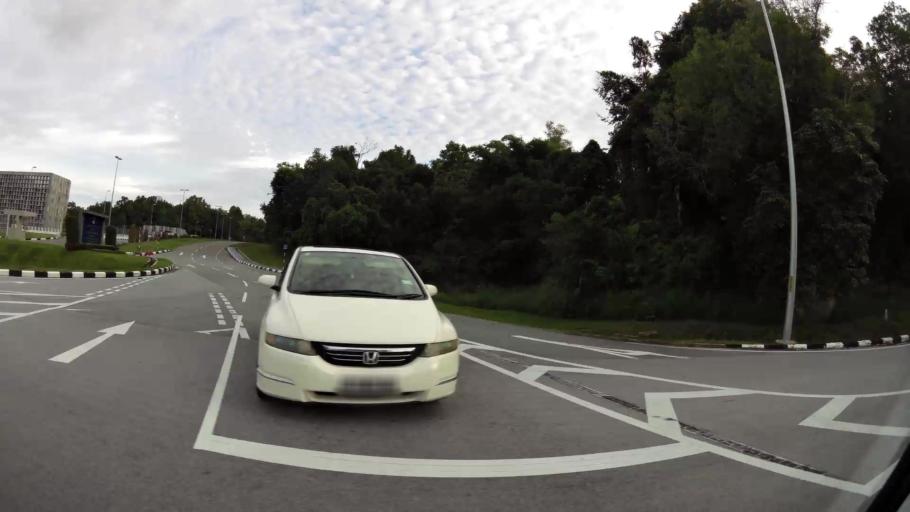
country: BN
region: Brunei and Muara
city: Bandar Seri Begawan
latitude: 4.9135
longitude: 114.9034
